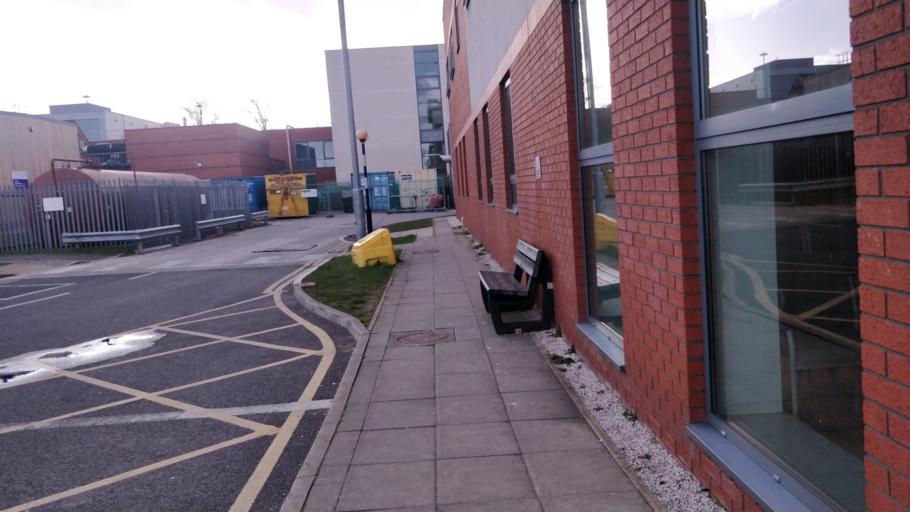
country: GB
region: England
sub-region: Knowsley
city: Huyton
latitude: 53.4114
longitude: -2.8992
